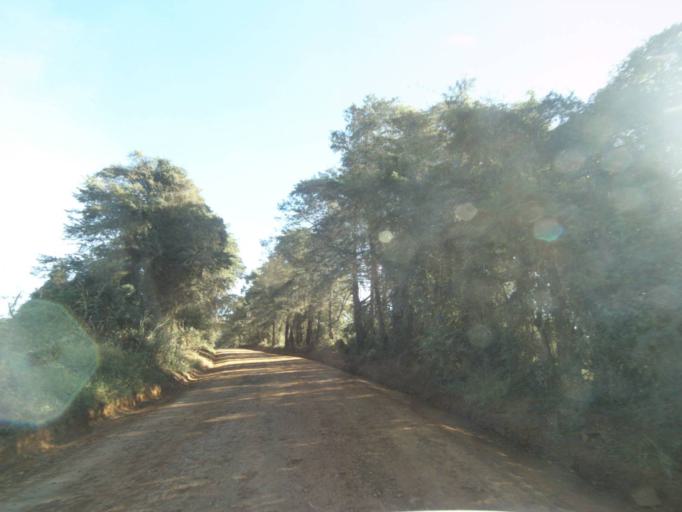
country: BR
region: Parana
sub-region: Tibagi
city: Tibagi
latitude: -24.5284
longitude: -50.5120
